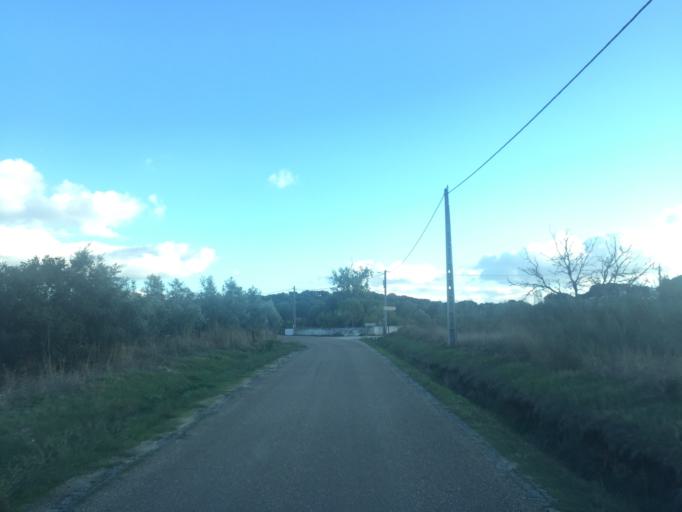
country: PT
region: Portalegre
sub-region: Alter do Chao
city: Alter do Chao
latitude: 39.1877
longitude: -7.6287
